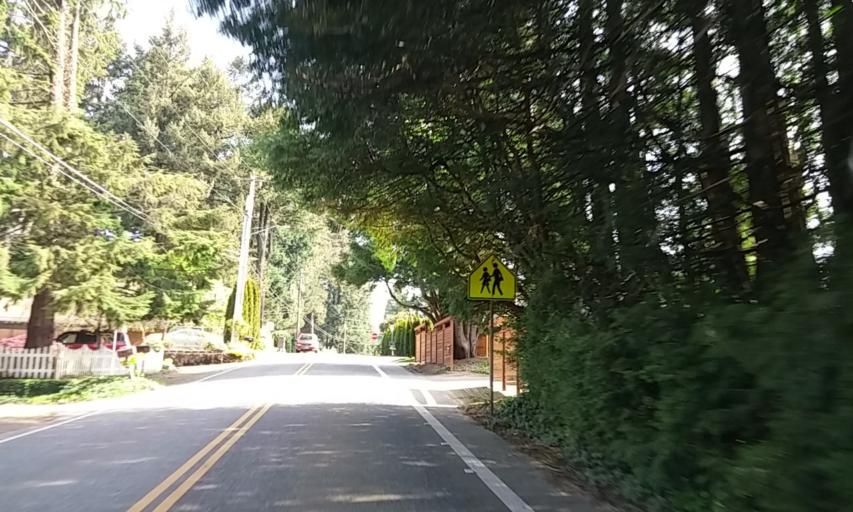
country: US
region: Oregon
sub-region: Washington County
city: West Slope
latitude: 45.5021
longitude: -122.7562
